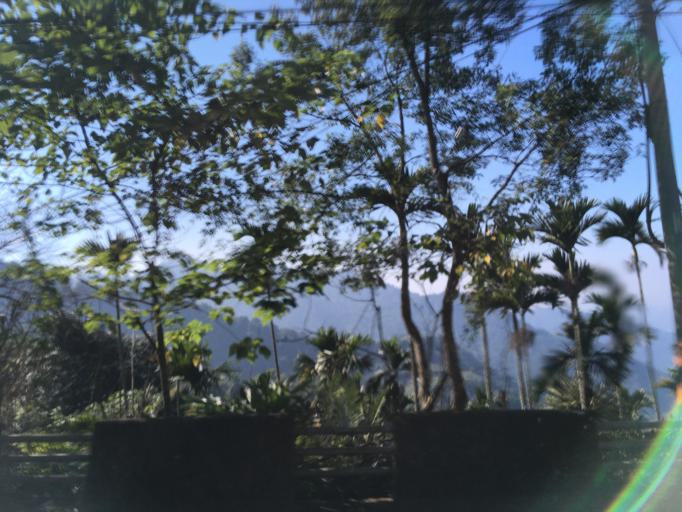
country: TW
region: Taiwan
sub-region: Chiayi
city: Jiayi Shi
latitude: 23.4083
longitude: 120.6496
